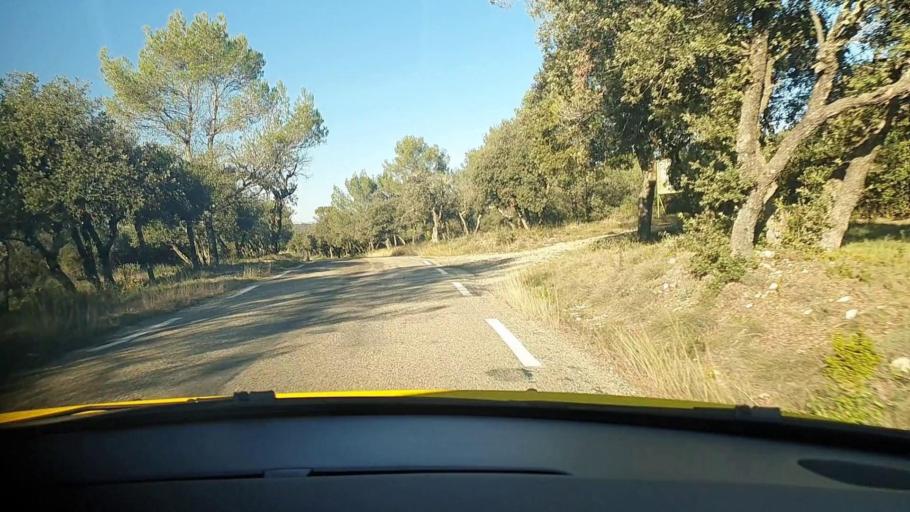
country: FR
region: Languedoc-Roussillon
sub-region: Departement du Gard
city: Goudargues
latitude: 44.1600
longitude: 4.3526
